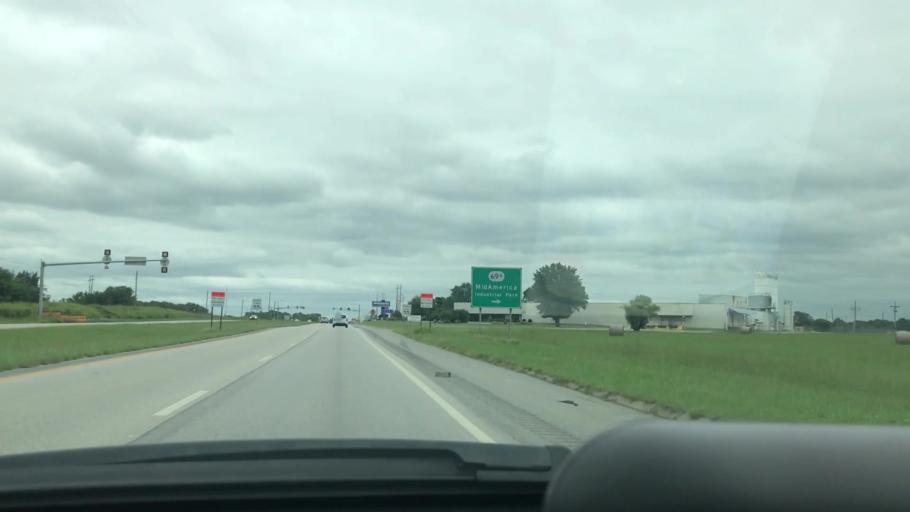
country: US
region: Oklahoma
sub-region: Mayes County
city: Chouteau
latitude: 36.2440
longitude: -95.3368
